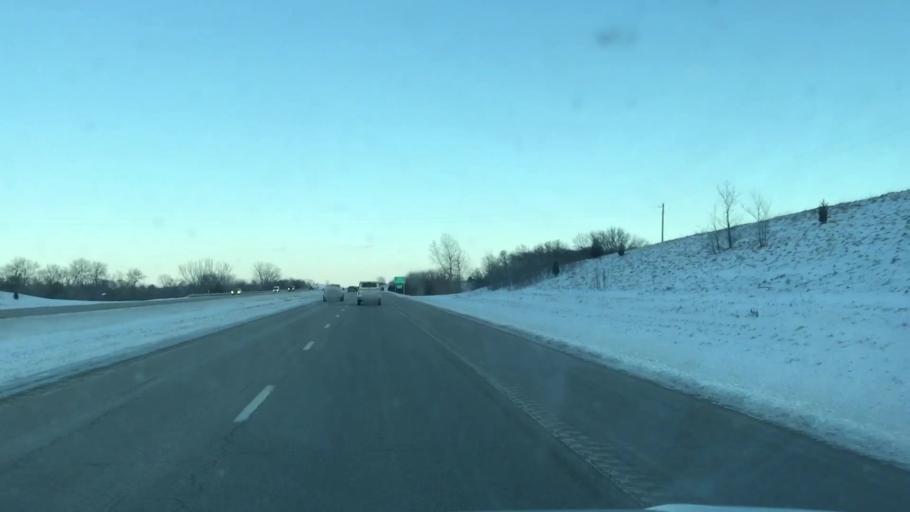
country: US
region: Missouri
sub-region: Buchanan County
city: Saint Joseph
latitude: 39.7476
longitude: -94.7053
